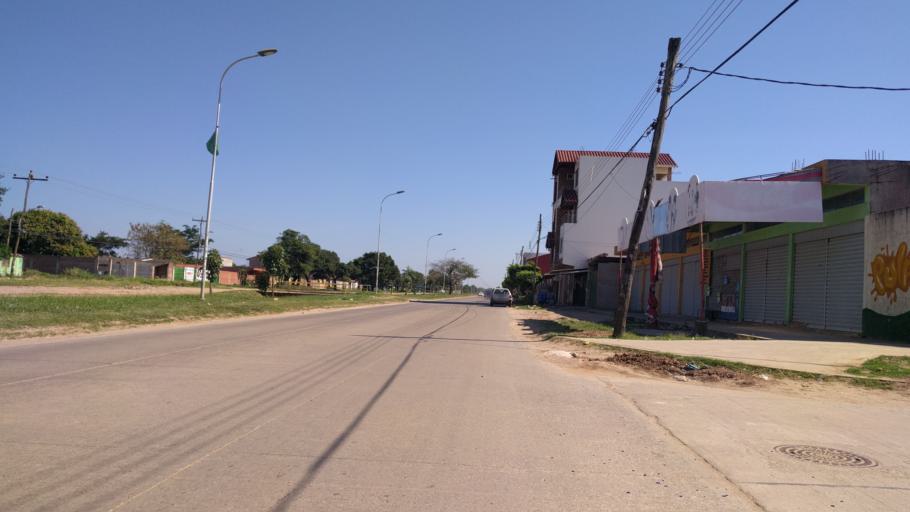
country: BO
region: Santa Cruz
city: Santa Cruz de la Sierra
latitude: -17.8576
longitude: -63.1887
